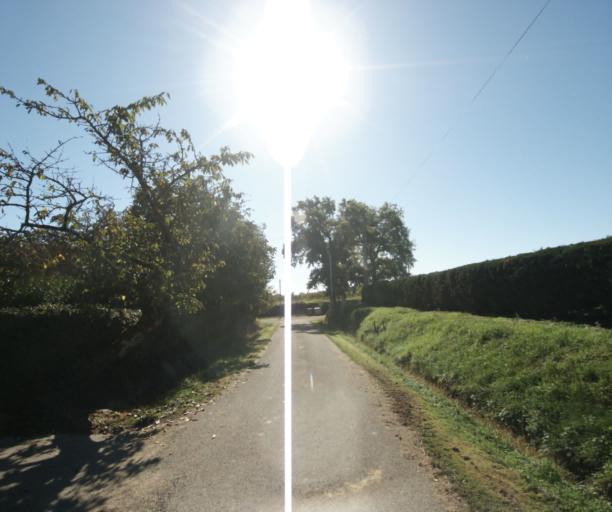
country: FR
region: Midi-Pyrenees
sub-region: Departement du Gers
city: Eauze
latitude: 43.8147
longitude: 0.1420
